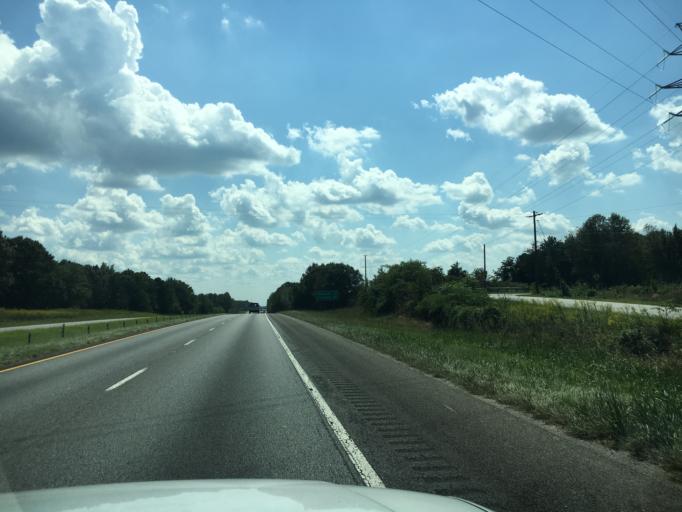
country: US
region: South Carolina
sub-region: Spartanburg County
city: Roebuck
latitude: 34.9125
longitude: -81.9901
